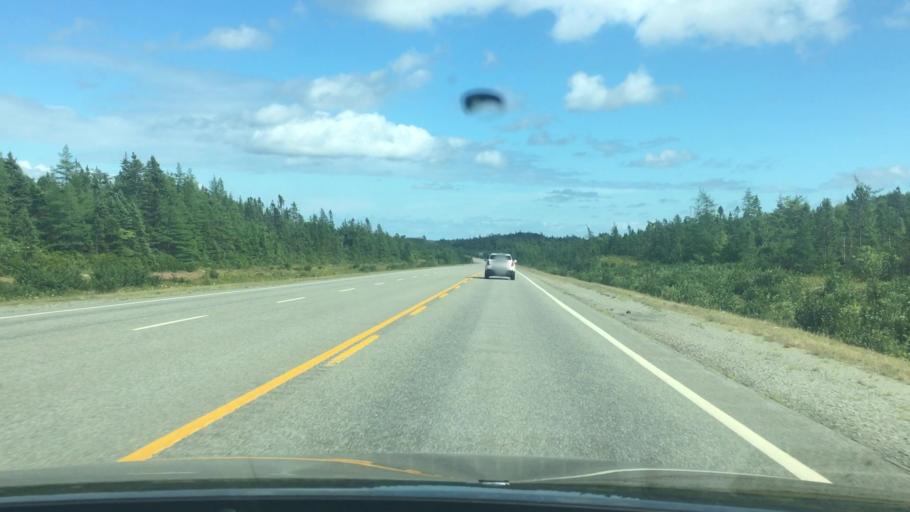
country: CA
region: Nova Scotia
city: Port Hawkesbury
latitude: 45.6177
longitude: -61.1058
